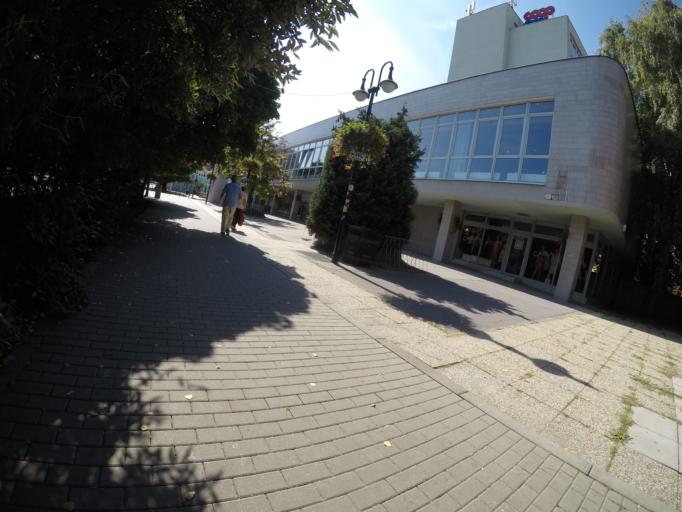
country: SK
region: Trnavsky
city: Dunajska Streda
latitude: 47.9951
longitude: 17.6153
